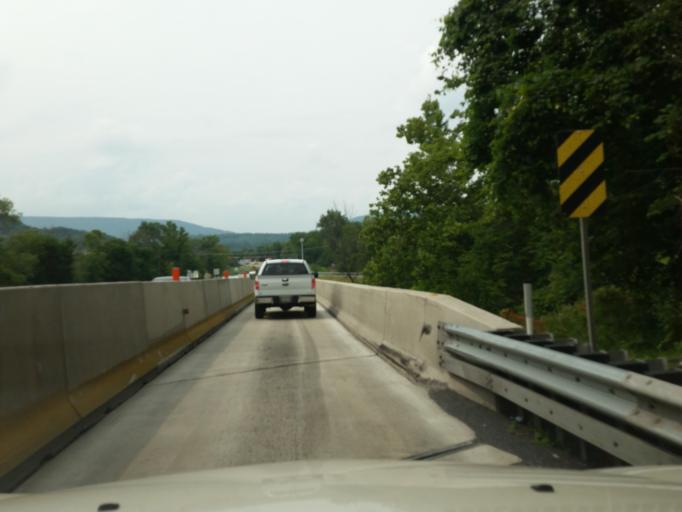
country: US
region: Pennsylvania
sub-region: Mifflin County
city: Lewistown
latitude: 40.5994
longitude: -77.5608
